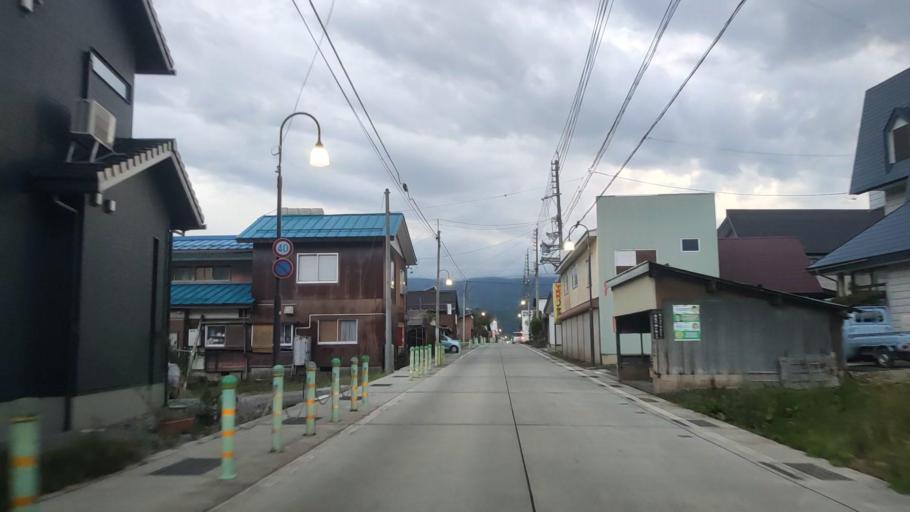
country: JP
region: Nagano
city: Iiyama
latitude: 36.8658
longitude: 138.4069
